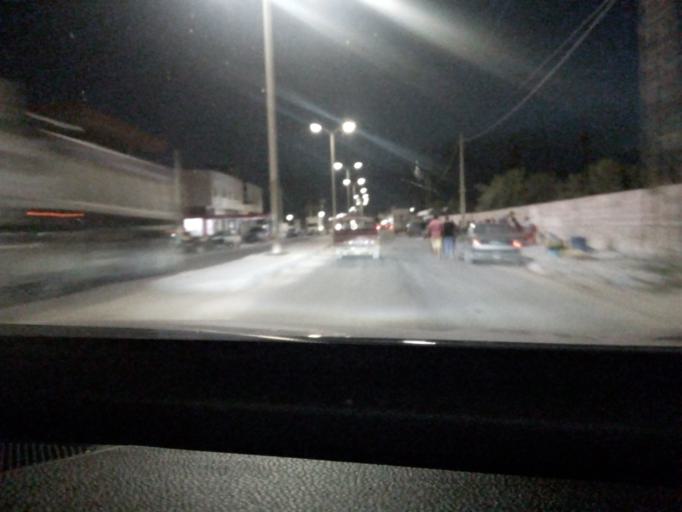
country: TN
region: Safaqis
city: Sfax
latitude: 34.7310
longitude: 10.6659
